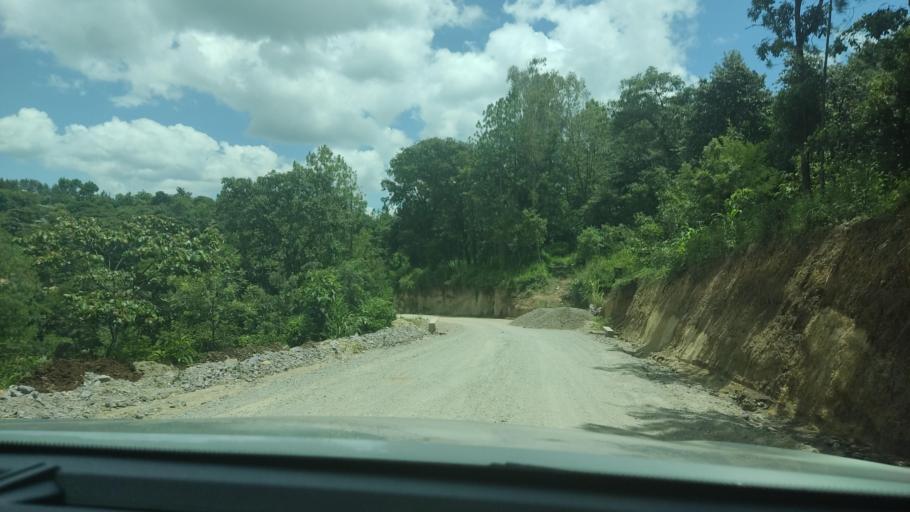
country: GT
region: Chimaltenango
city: San Martin Jilotepeque
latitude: 14.7961
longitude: -90.8121
